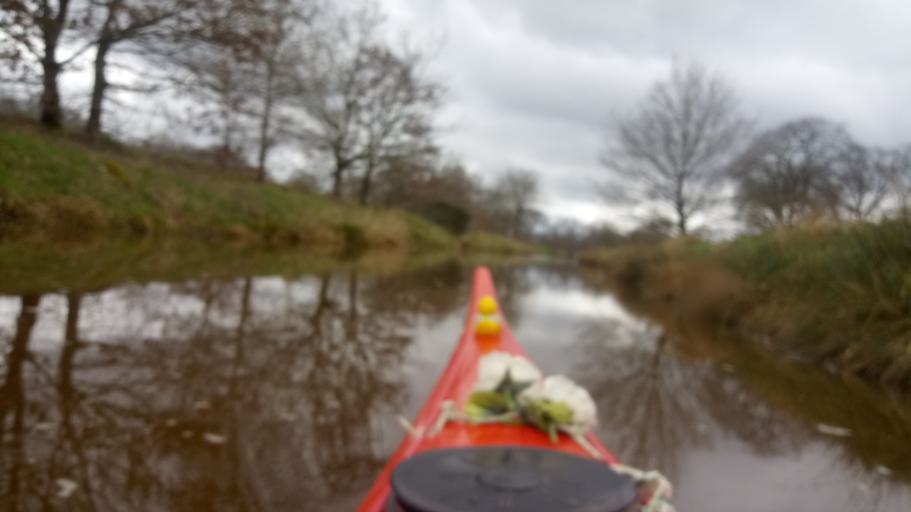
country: NL
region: Groningen
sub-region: Gemeente Vlagtwedde
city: Sellingen
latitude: 52.9370
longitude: 7.1300
